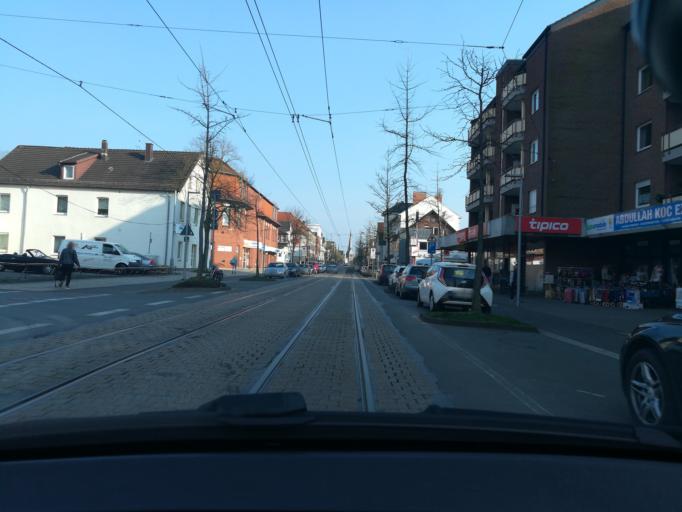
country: DE
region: North Rhine-Westphalia
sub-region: Regierungsbezirk Detmold
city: Bielefeld
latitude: 51.9935
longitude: 8.5073
